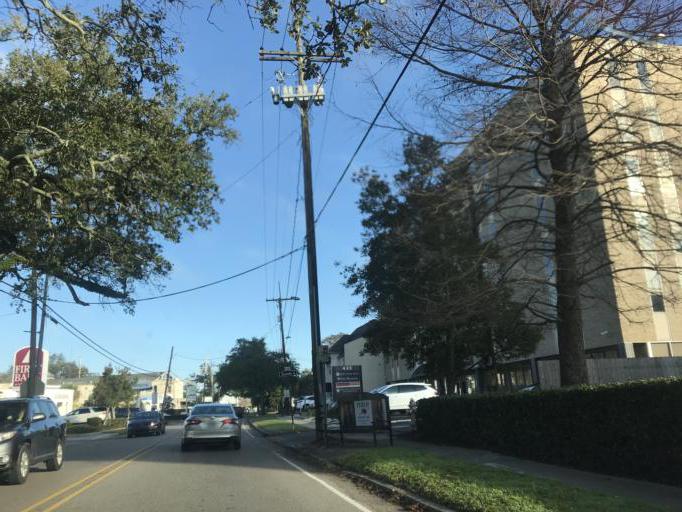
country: US
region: Louisiana
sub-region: Jefferson Parish
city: Metairie
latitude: 29.9842
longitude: -90.1288
